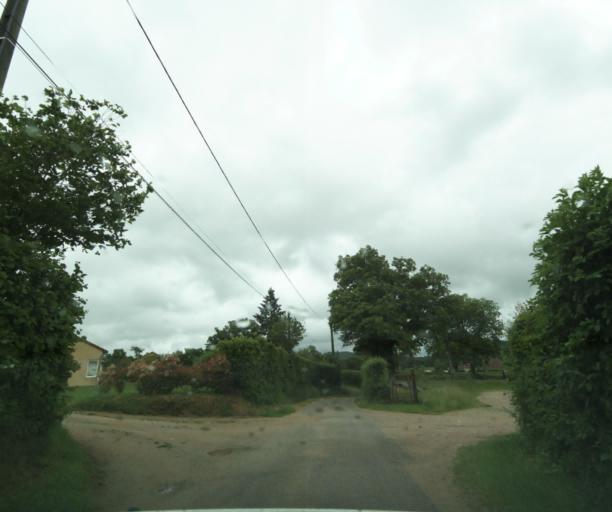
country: FR
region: Bourgogne
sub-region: Departement de Saone-et-Loire
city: Charolles
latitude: 46.4406
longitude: 4.4238
